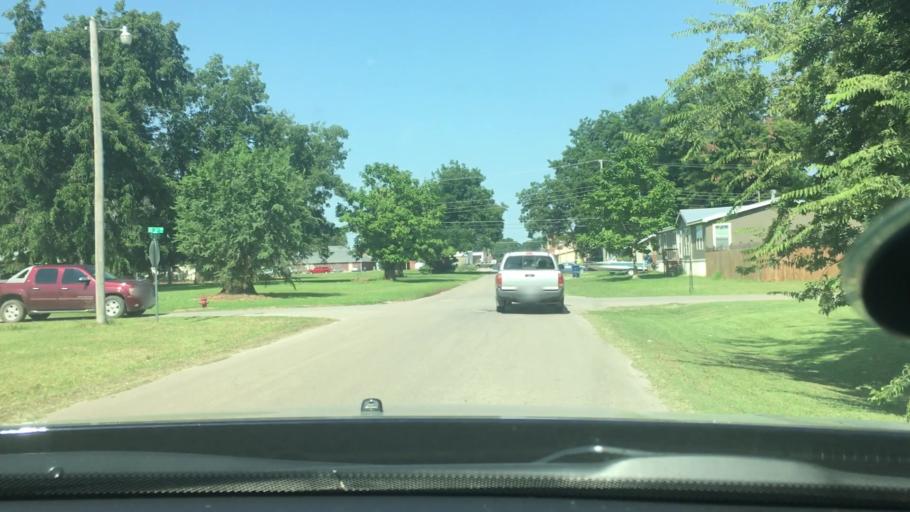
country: US
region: Oklahoma
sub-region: Garvin County
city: Lindsay
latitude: 34.8336
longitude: -97.5996
